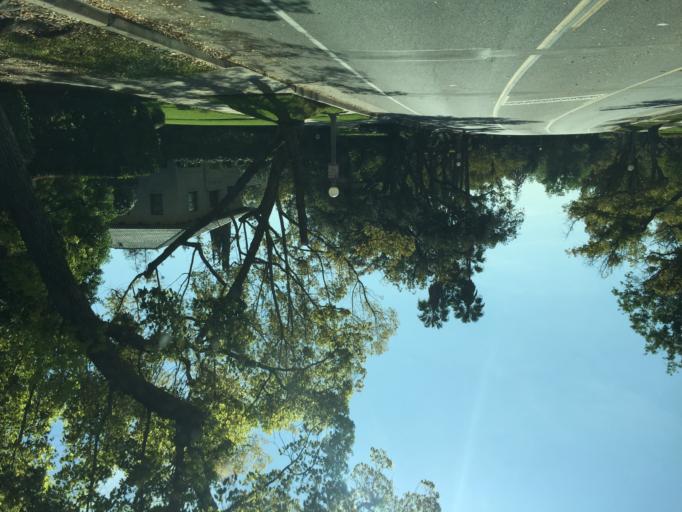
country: US
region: California
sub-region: Los Angeles County
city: South Pasadena
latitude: 34.1238
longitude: -118.1358
